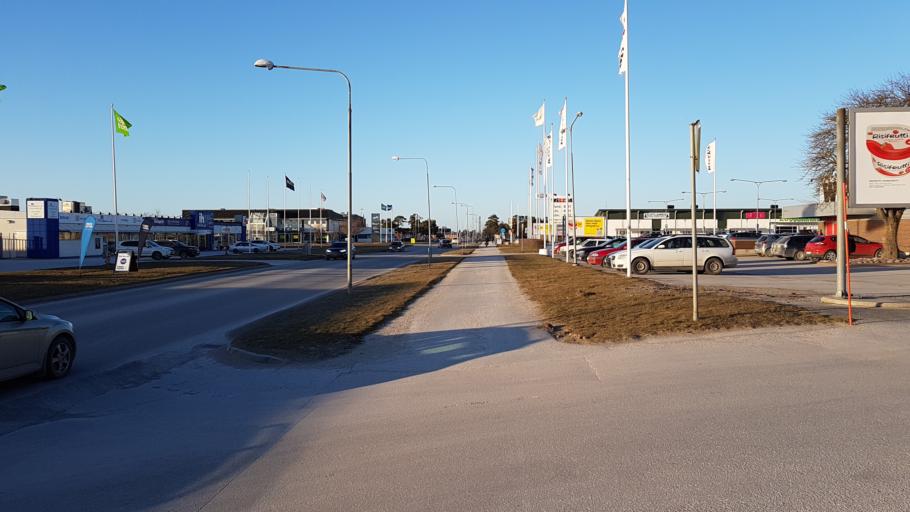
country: SE
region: Gotland
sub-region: Gotland
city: Visby
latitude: 57.6349
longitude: 18.3265
